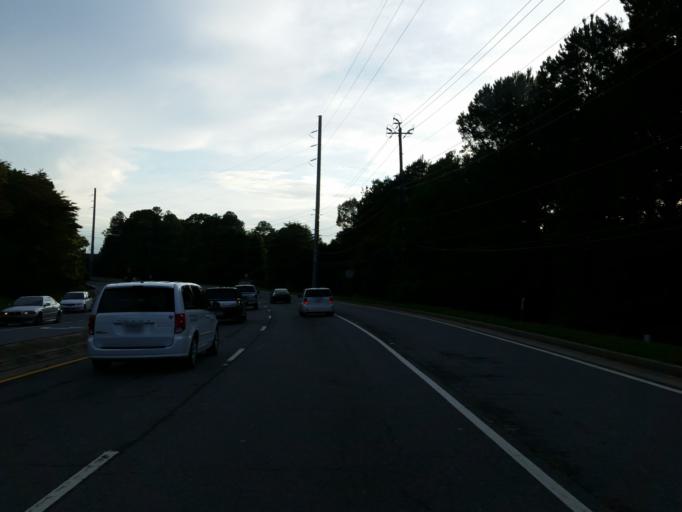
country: US
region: Georgia
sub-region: Fulton County
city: Roswell
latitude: 34.0011
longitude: -84.4036
